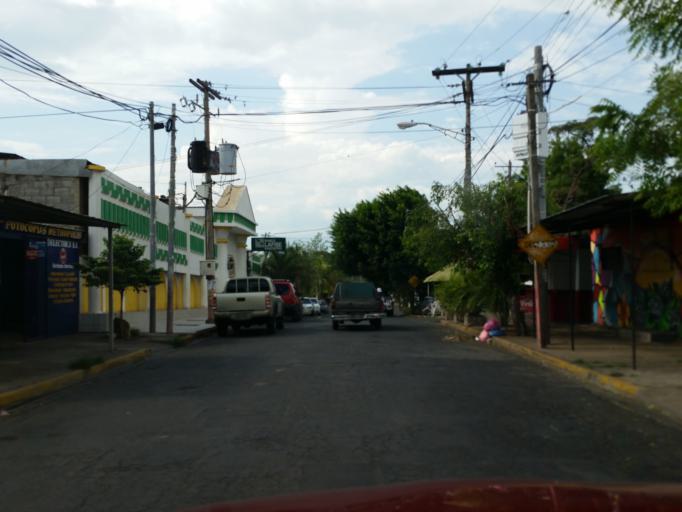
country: NI
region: Managua
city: Managua
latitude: 12.1222
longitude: -86.2492
